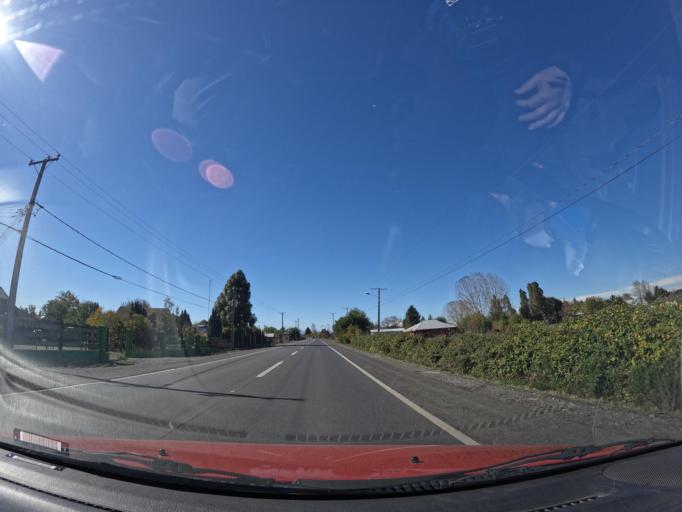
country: CL
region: Biobio
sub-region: Provincia de Nuble
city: Chillan
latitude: -36.6442
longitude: -72.0516
